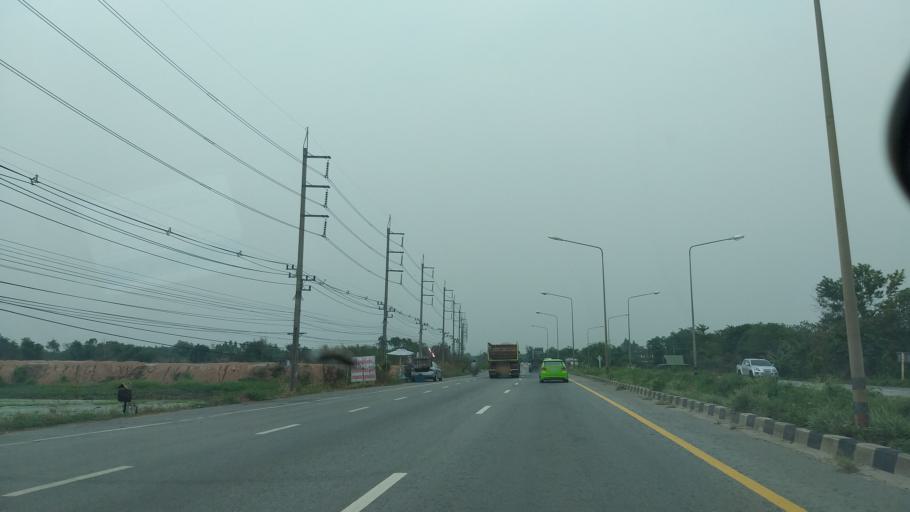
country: TH
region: Chon Buri
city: Ko Chan
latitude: 13.3978
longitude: 101.2812
